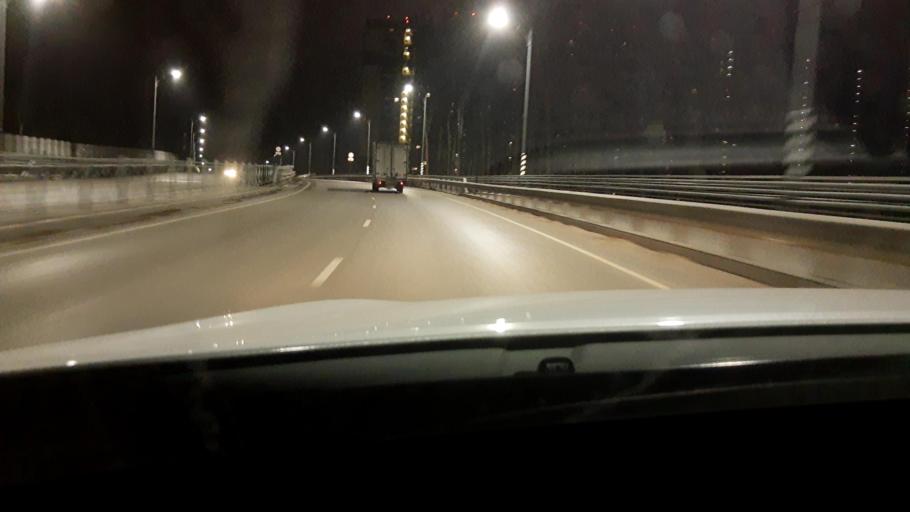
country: RU
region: Moskovskaya
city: Reutov
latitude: 55.7591
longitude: 37.8836
